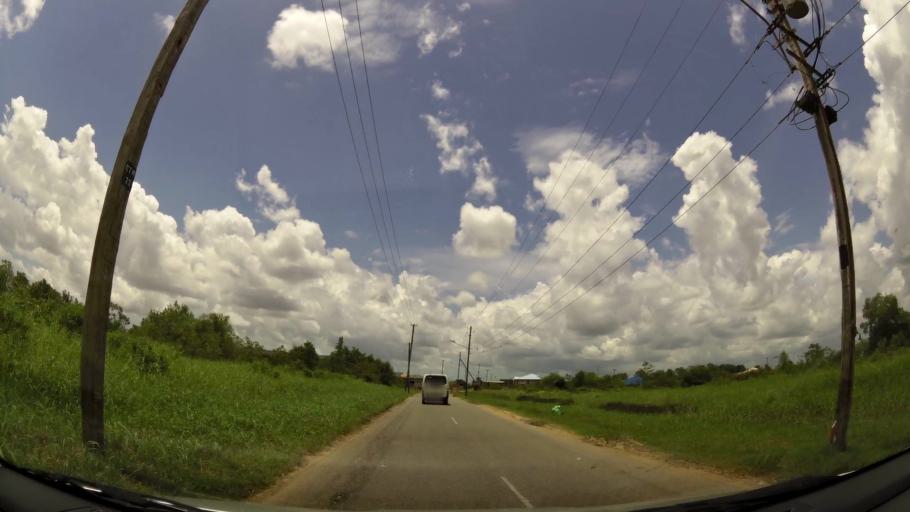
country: SR
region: Commewijne
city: Nieuw Amsterdam
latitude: 5.8261
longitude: -55.0998
